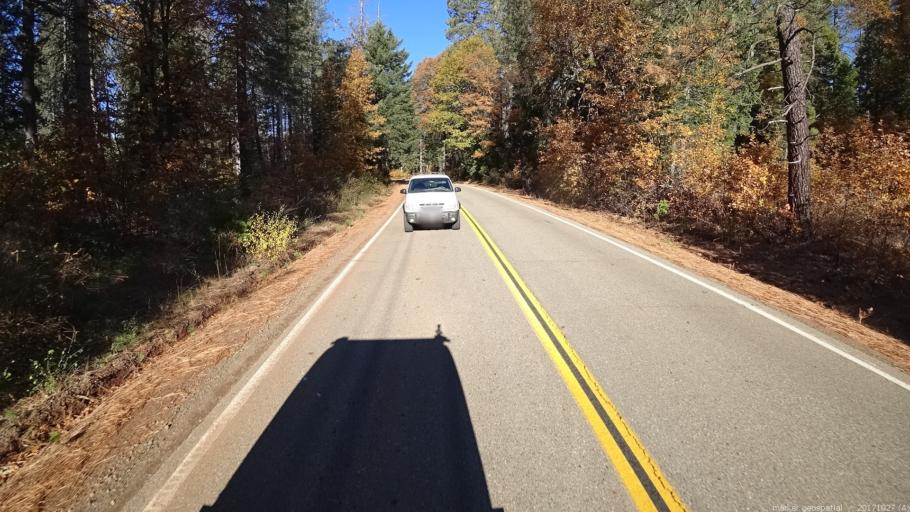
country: US
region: California
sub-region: Shasta County
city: Burney
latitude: 40.9333
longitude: -121.9472
